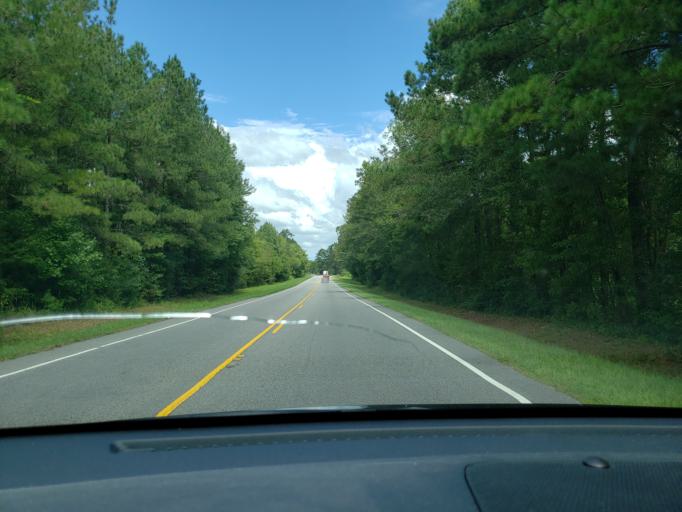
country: US
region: North Carolina
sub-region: Columbus County
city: Brunswick
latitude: 34.2334
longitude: -78.7529
